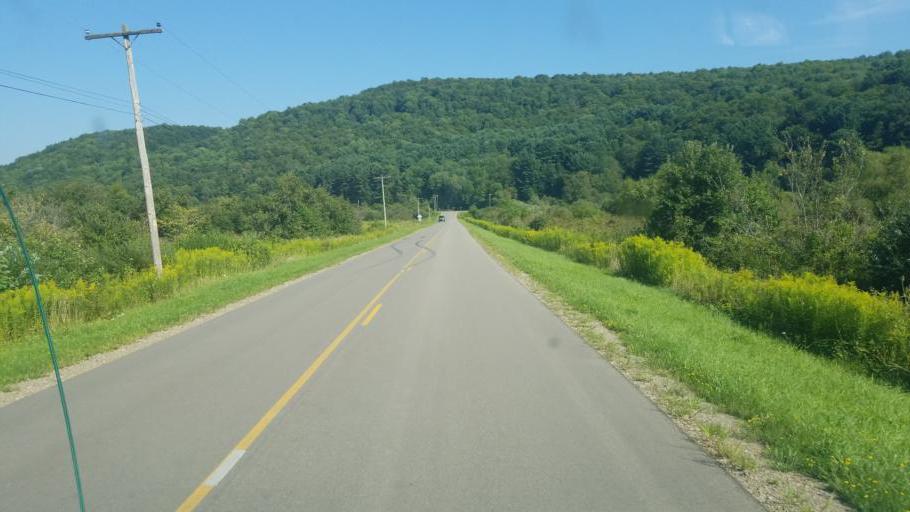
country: US
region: New York
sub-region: Allegany County
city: Wellsville
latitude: 42.0242
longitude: -77.9526
